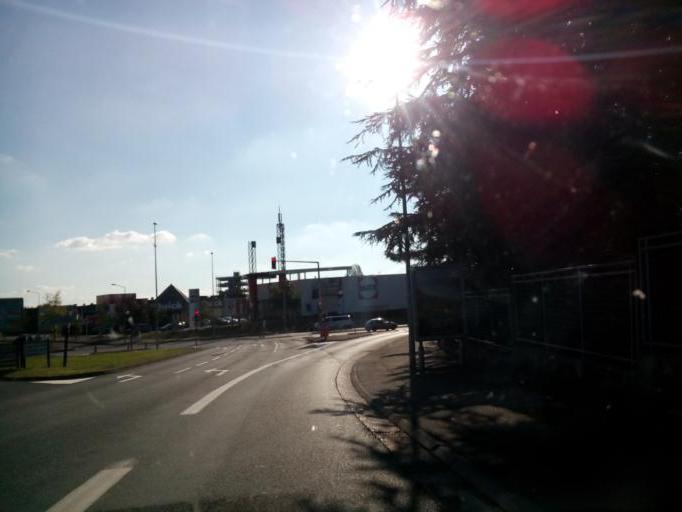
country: FR
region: Rhone-Alpes
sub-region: Departement du Rhone
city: Bron
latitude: 45.7236
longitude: 4.9207
